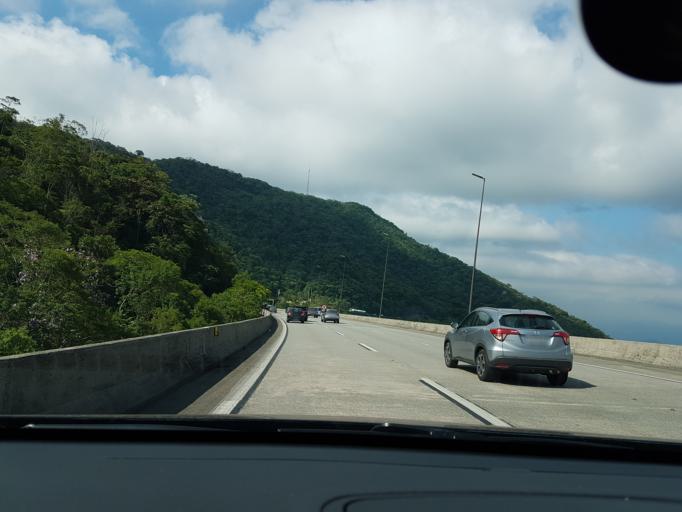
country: BR
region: Sao Paulo
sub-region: Cubatao
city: Cubatao
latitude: -23.9226
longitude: -46.5322
